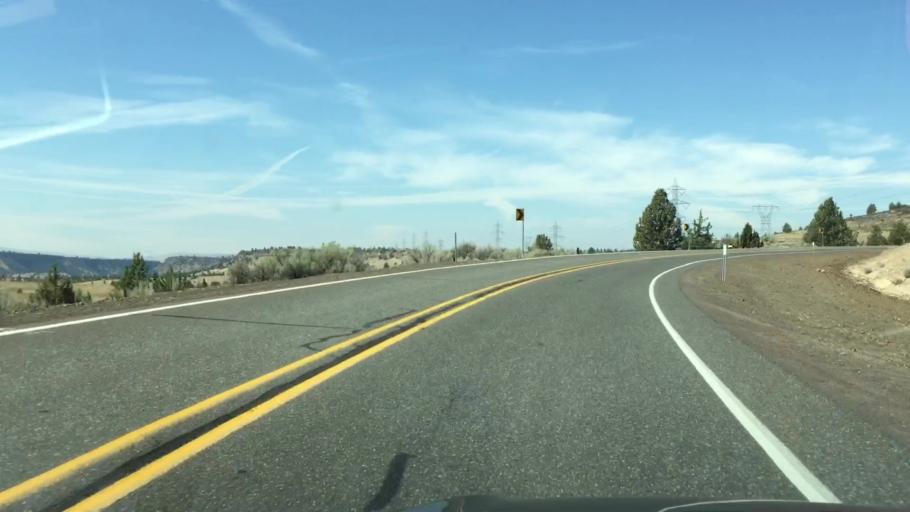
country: US
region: Oregon
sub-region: Wasco County
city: The Dalles
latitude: 45.1682
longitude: -121.1035
